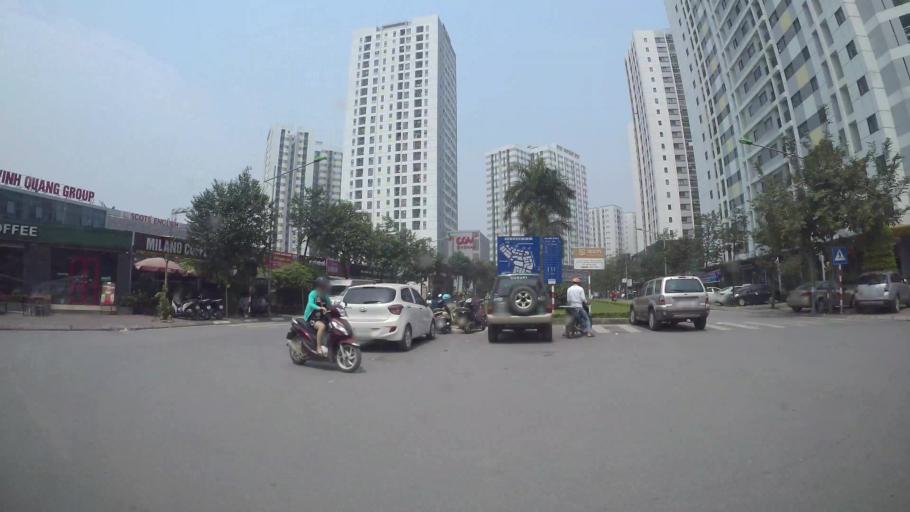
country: VN
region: Ha Noi
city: Van Dien
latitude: 20.9634
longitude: 105.8244
